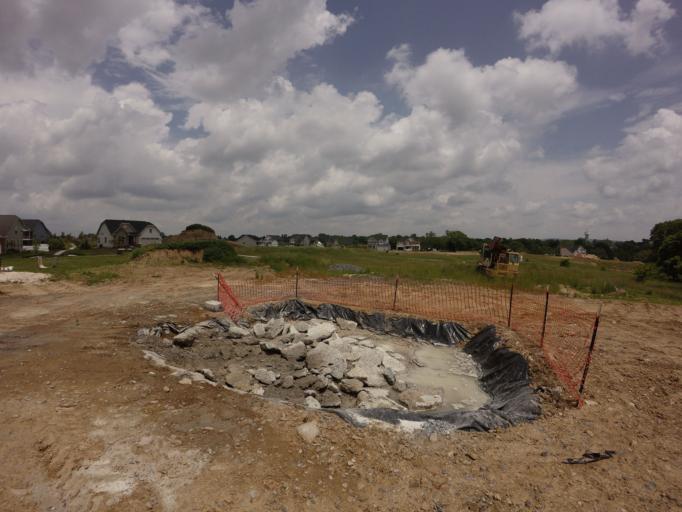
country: US
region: Maryland
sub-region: Frederick County
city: Brunswick
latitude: 39.3239
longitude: -77.6321
